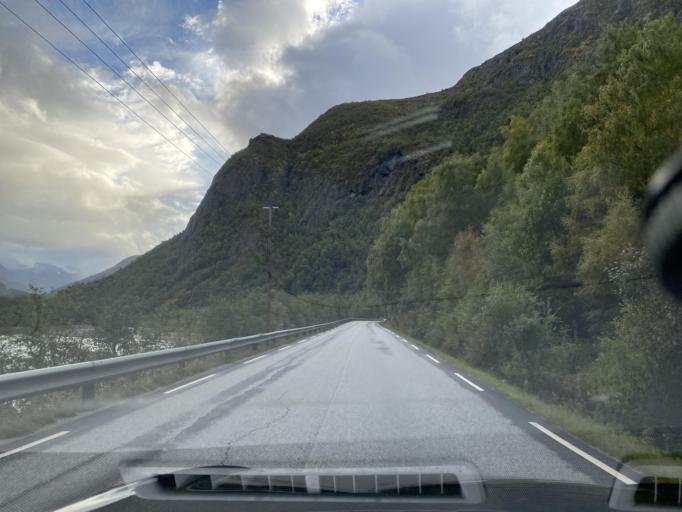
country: NO
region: Oppland
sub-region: Lom
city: Fossbergom
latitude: 61.7823
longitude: 8.4359
